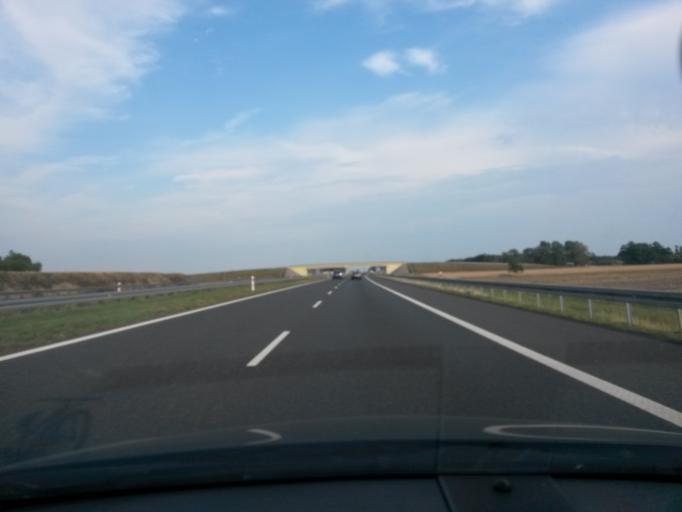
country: PL
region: Lodz Voivodeship
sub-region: Powiat zgierski
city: Parzeczew
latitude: 51.9500
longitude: 19.1616
